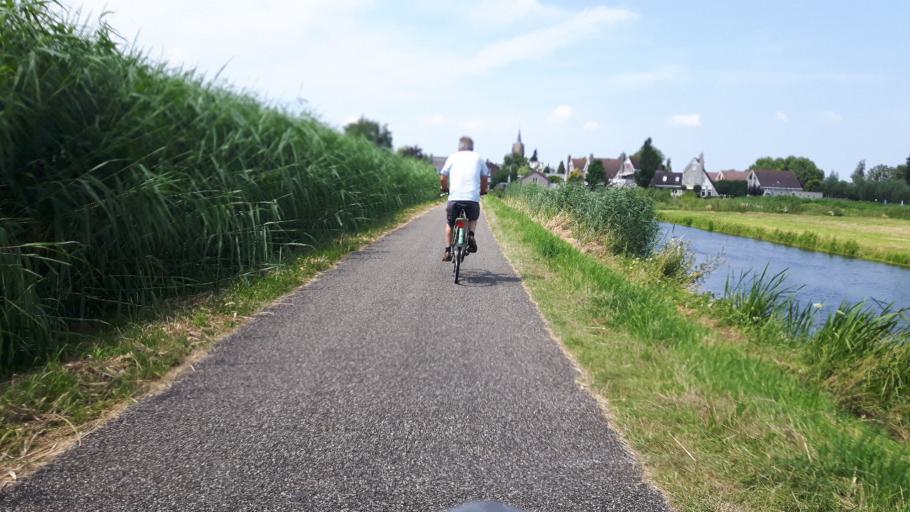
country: NL
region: South Holland
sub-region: Molenwaard
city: Liesveld
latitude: 51.9195
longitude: 4.8214
